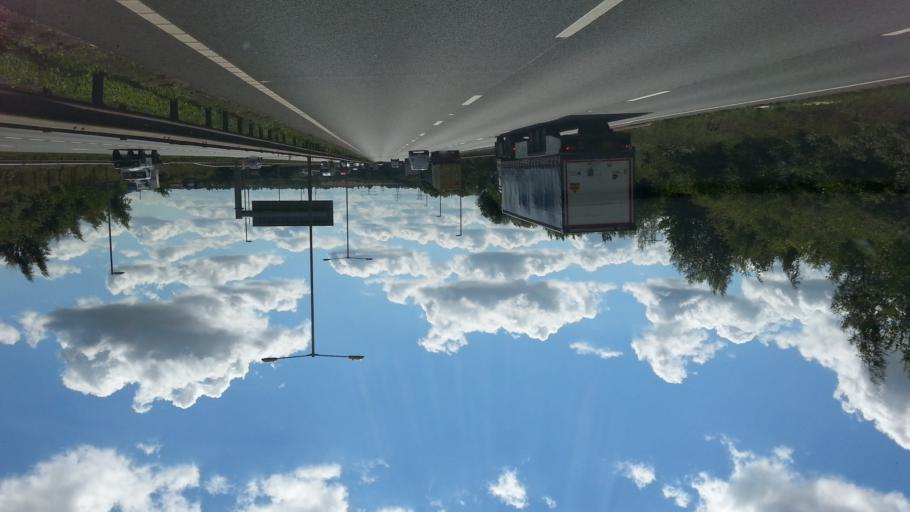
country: GB
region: England
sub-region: Northamptonshire
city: Kettering
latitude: 52.4026
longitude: -0.7512
